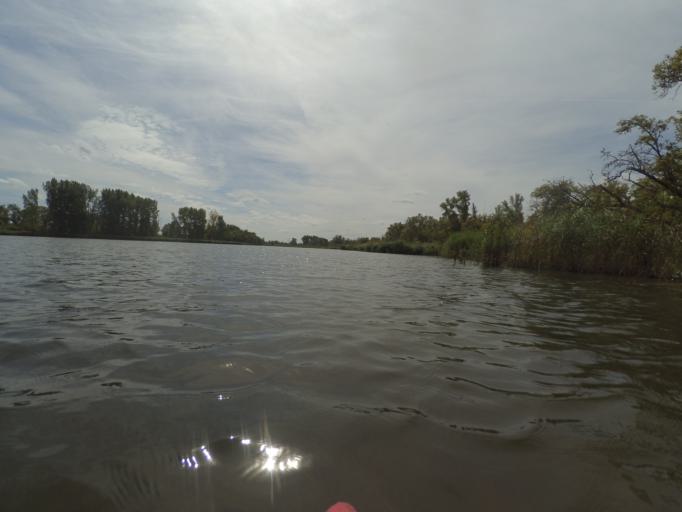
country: NL
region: North Brabant
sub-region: Gemeente Geertruidenberg
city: Geertruidenberg
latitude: 51.7405
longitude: 4.8492
